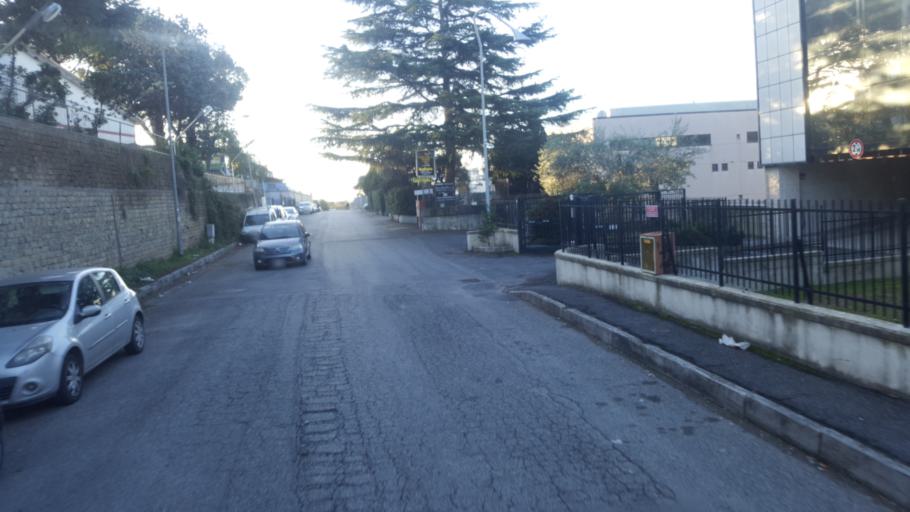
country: IT
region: Latium
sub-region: Citta metropolitana di Roma Capitale
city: Formello
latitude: 42.0523
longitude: 12.4025
